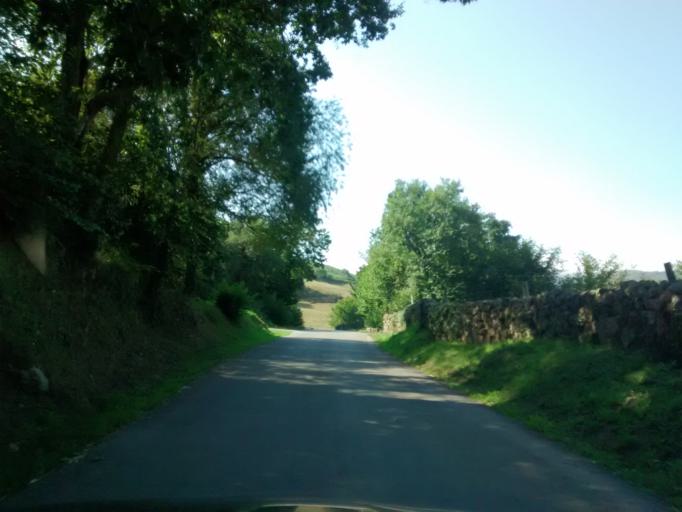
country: ES
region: Cantabria
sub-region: Provincia de Cantabria
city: Ruente
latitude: 43.2506
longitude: -4.2441
